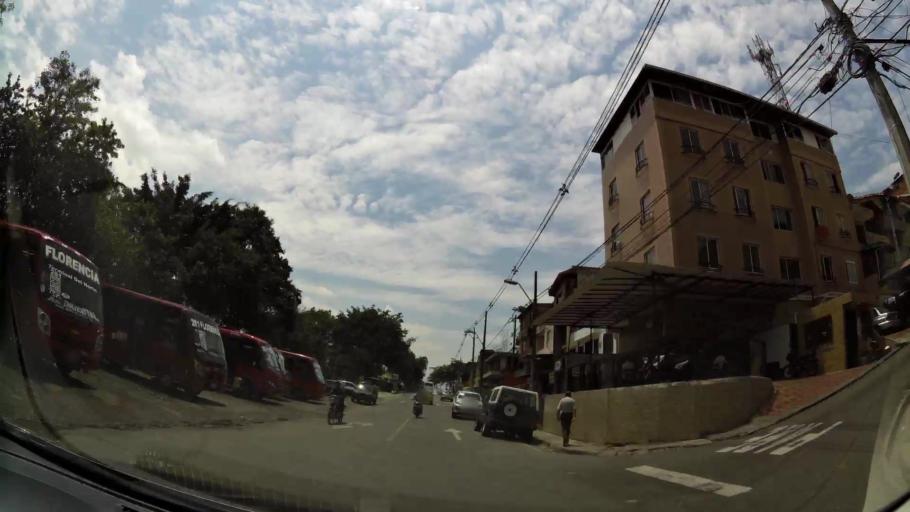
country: CO
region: Antioquia
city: Bello
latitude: 6.3062
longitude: -75.5707
